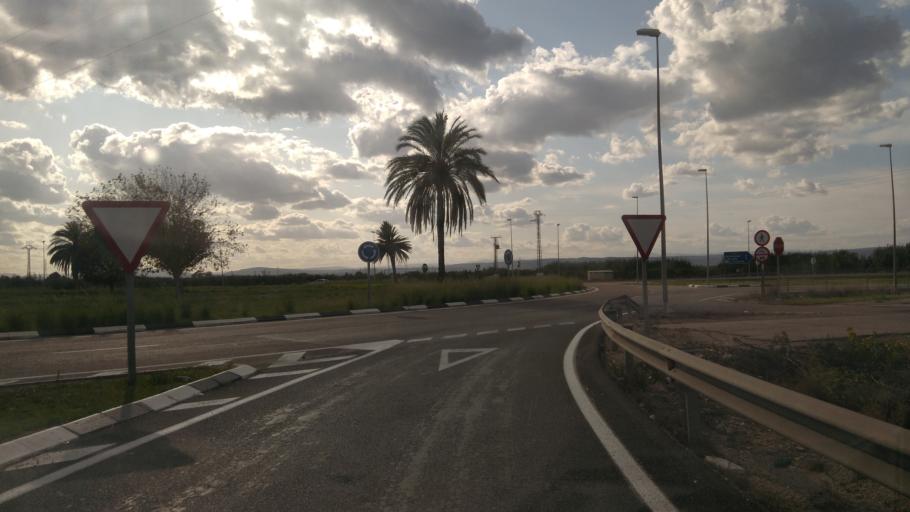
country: ES
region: Valencia
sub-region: Provincia de Valencia
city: Guadassuar
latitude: 39.1623
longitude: -0.4551
